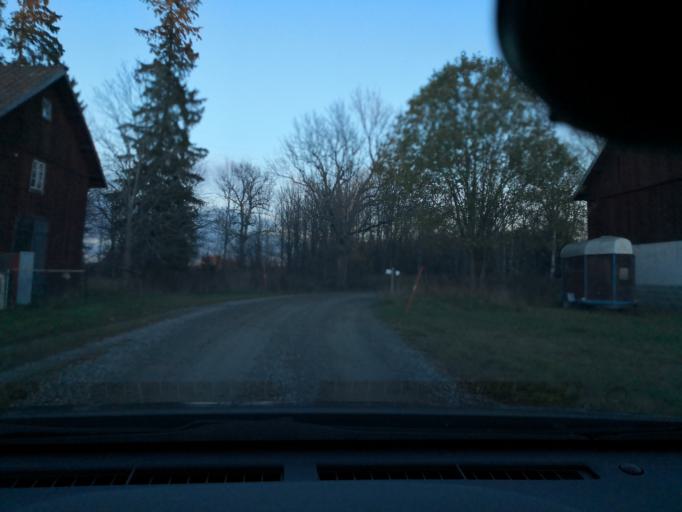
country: SE
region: Vaestmanland
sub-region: Vasteras
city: Tillberga
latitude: 59.7639
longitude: 16.6195
